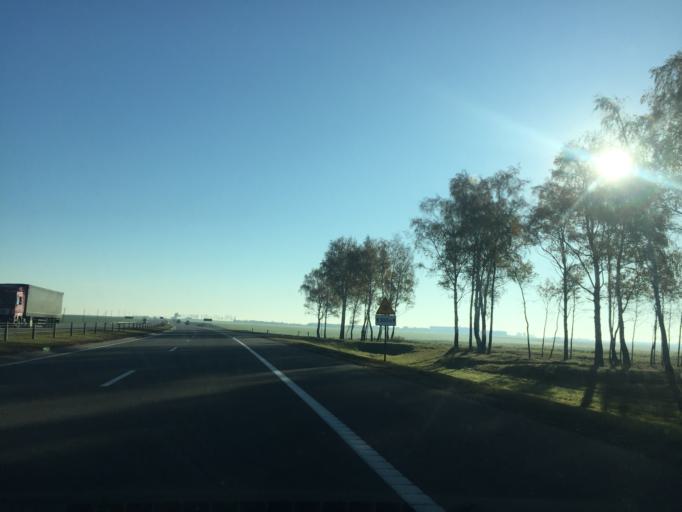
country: BY
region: Minsk
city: Luhavaya Slabada
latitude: 53.7615
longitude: 27.8839
